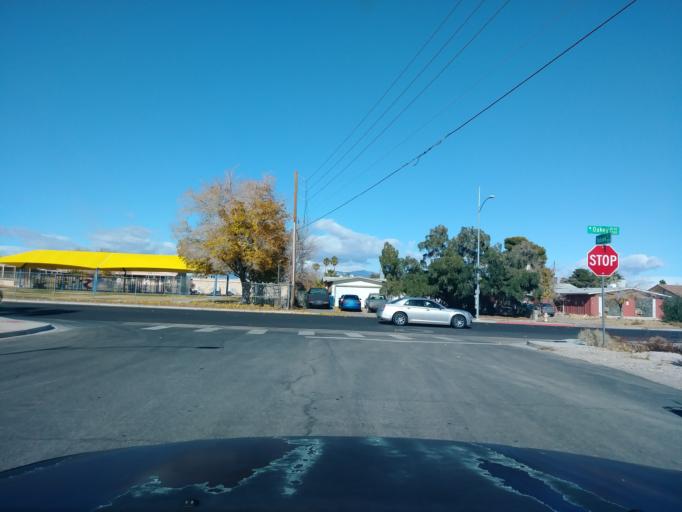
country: US
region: Nevada
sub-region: Clark County
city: Spring Valley
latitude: 36.1514
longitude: -115.2147
